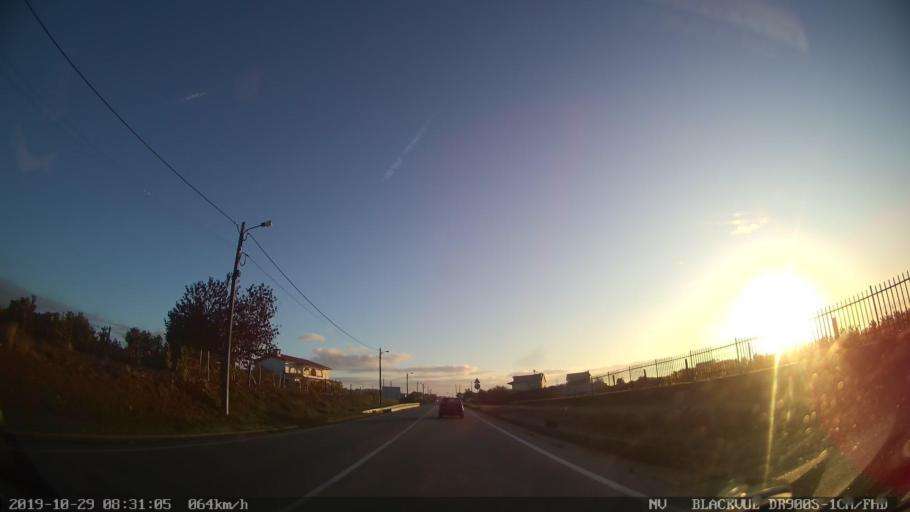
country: PT
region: Vila Real
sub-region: Sabrosa
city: Sabrosa
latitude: 41.2626
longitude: -7.5996
